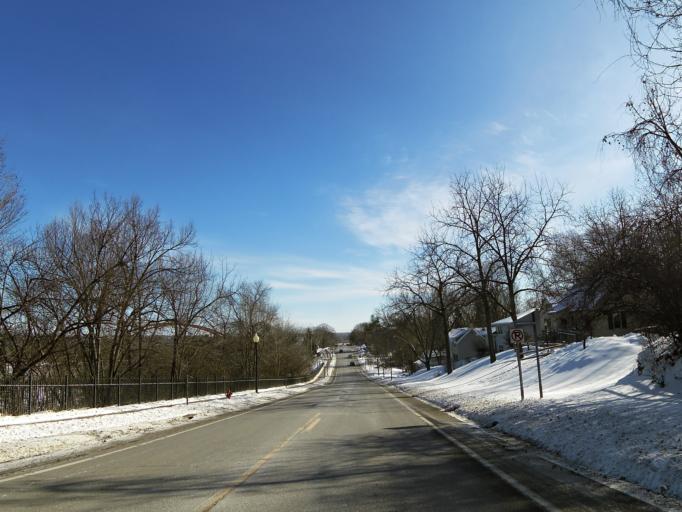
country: US
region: Minnesota
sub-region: Dakota County
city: Hastings
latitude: 44.7443
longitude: -92.8606
